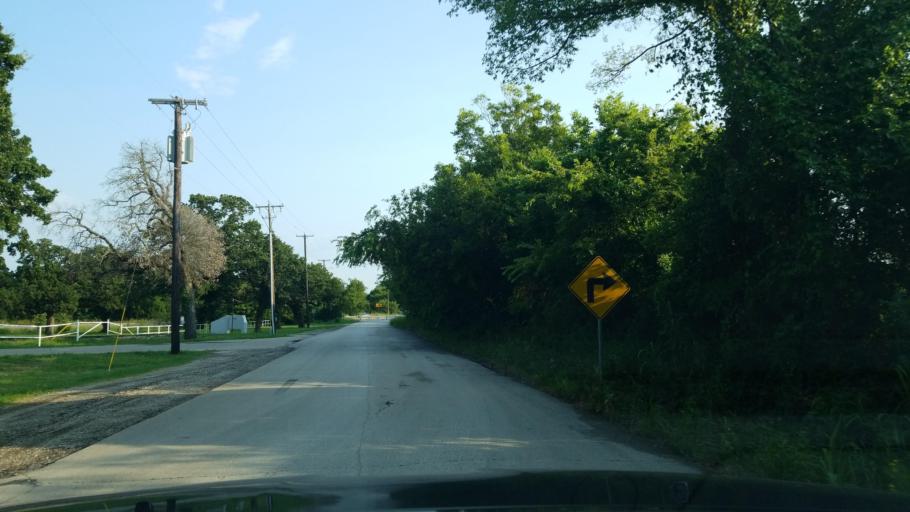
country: US
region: Texas
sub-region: Denton County
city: Cross Roads
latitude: 33.2483
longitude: -97.0616
